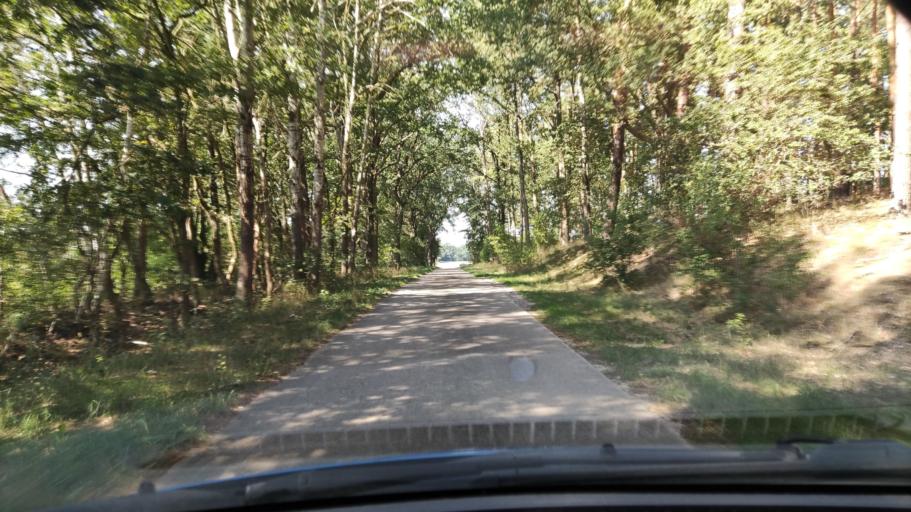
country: DE
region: Lower Saxony
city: Gohrde
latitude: 53.1409
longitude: 10.9459
